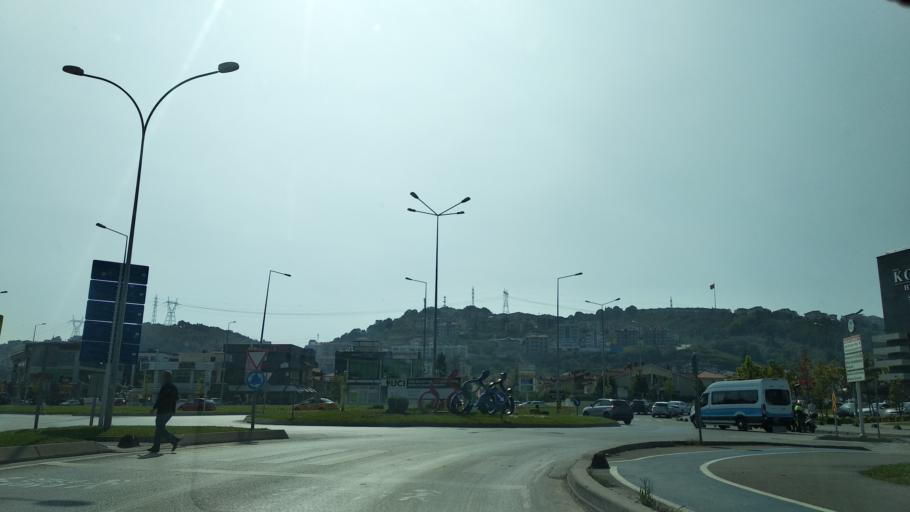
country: TR
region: Sakarya
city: Adapazari
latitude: 40.7608
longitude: 30.3630
